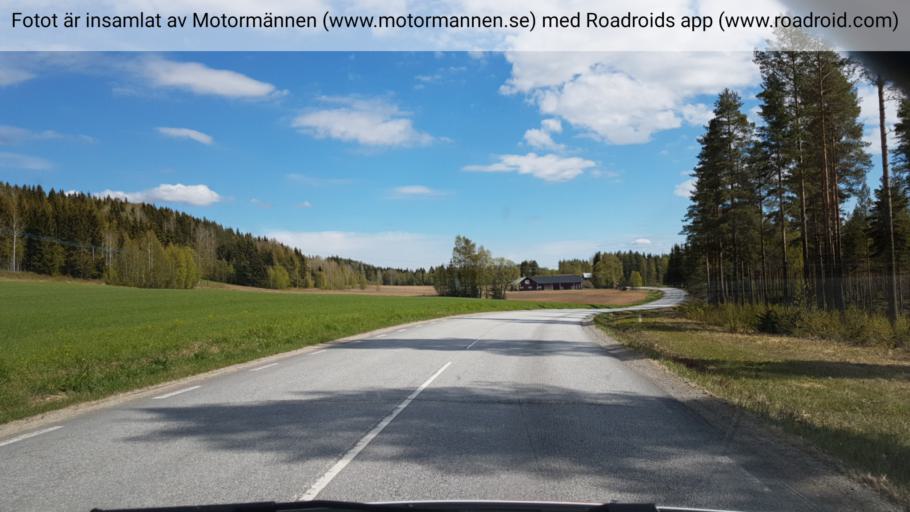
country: SE
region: Vaesterbotten
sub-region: Vindelns Kommun
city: Vindeln
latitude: 64.1797
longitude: 19.7195
